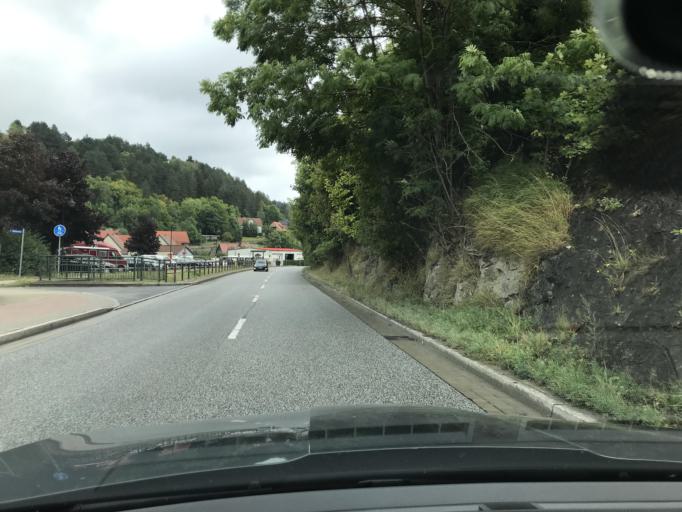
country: DE
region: Saxony-Anhalt
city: Rubeland
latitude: 51.7587
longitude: 10.8364
